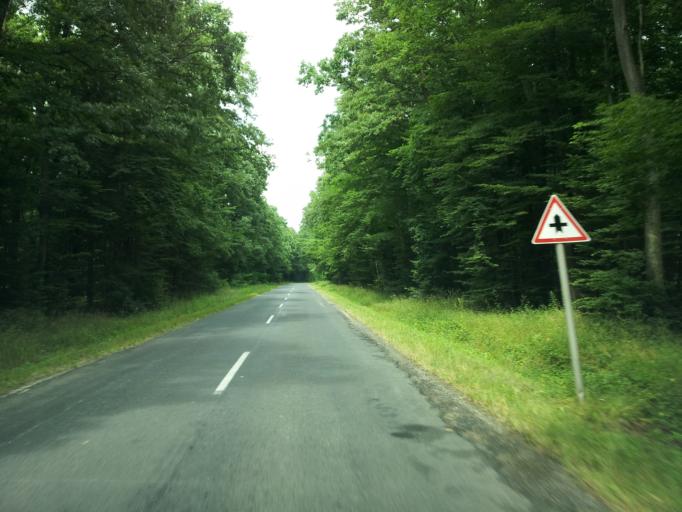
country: HU
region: Zala
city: Turje
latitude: 47.0727
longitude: 17.0185
